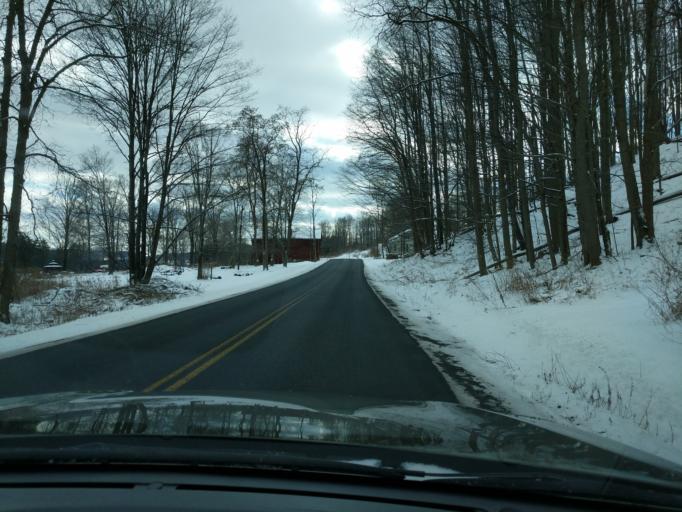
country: US
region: New York
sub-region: Tompkins County
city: East Ithaca
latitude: 42.4046
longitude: -76.3797
